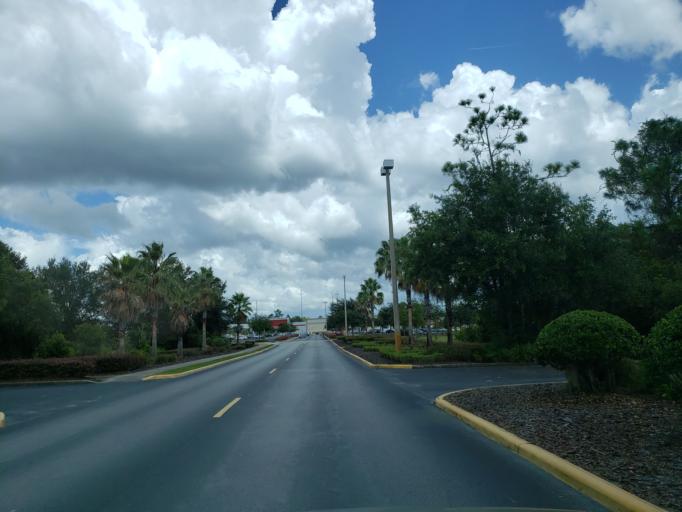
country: US
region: Florida
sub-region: Hillsborough County
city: Pebble Creek
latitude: 28.1152
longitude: -82.3768
